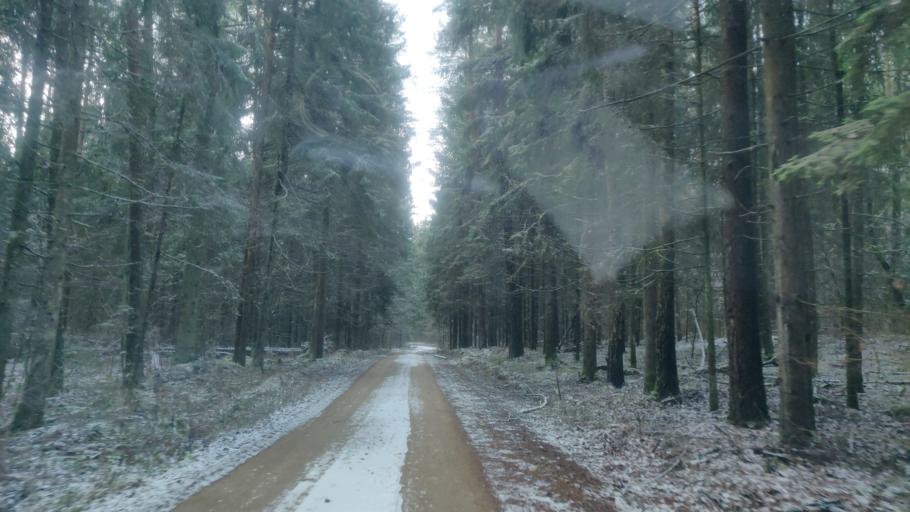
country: LT
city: Trakai
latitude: 54.5780
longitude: 24.9454
